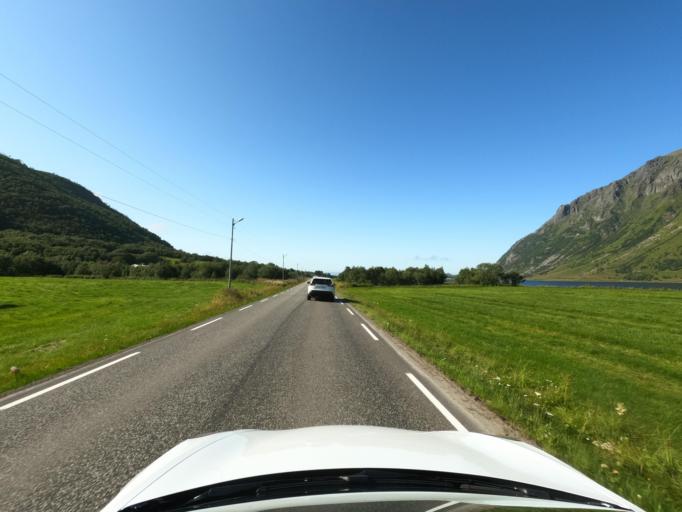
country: NO
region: Nordland
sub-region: Vestvagoy
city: Evjen
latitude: 68.2765
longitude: 13.9269
